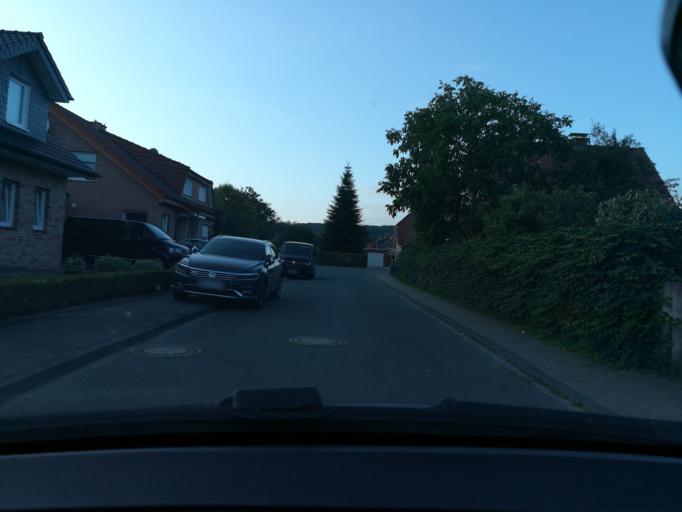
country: DE
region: North Rhine-Westphalia
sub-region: Regierungsbezirk Munster
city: Lienen
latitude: 52.1433
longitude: 7.9758
